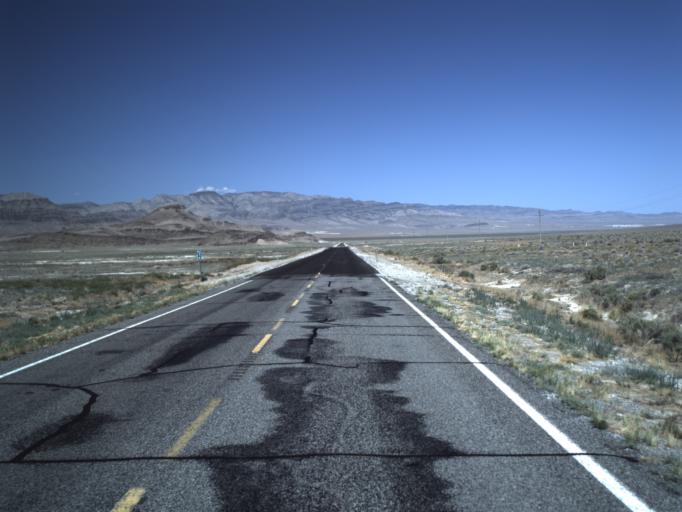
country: US
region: Utah
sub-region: Beaver County
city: Milford
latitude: 39.0472
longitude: -113.4132
